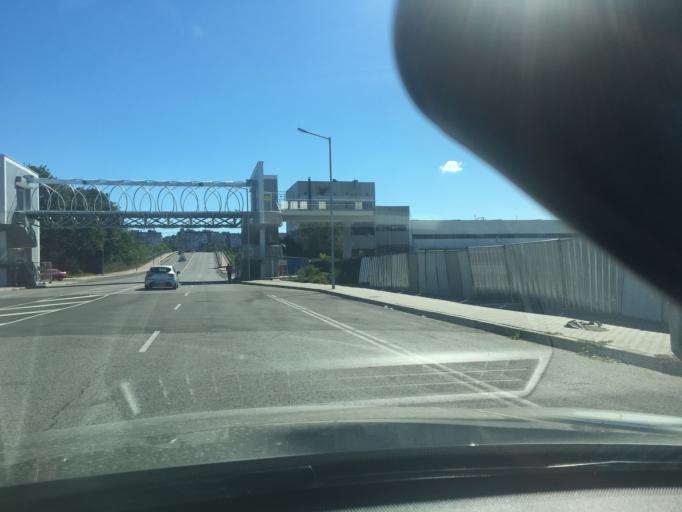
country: BG
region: Burgas
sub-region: Obshtina Burgas
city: Burgas
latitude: 42.5116
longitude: 27.4589
